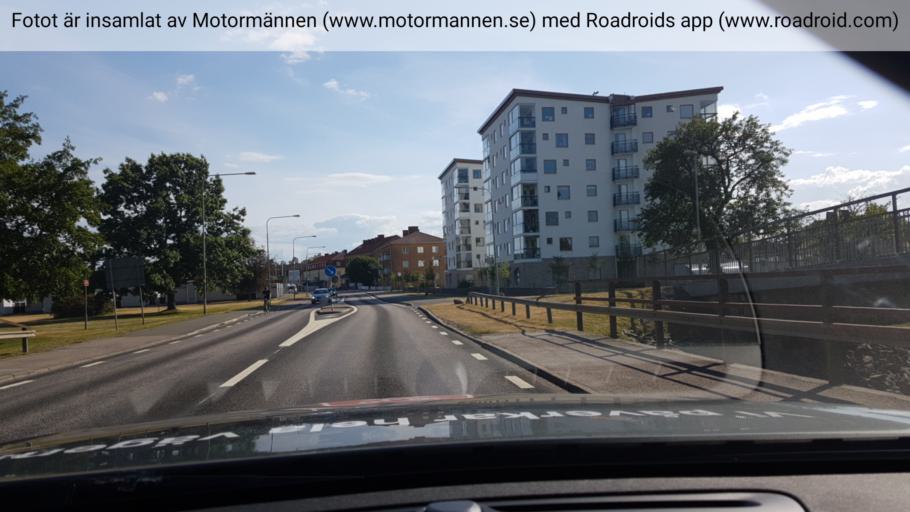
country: SE
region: Vaestra Goetaland
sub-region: Karlsborgs Kommun
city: Karlsborg
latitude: 58.5394
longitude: 14.5064
